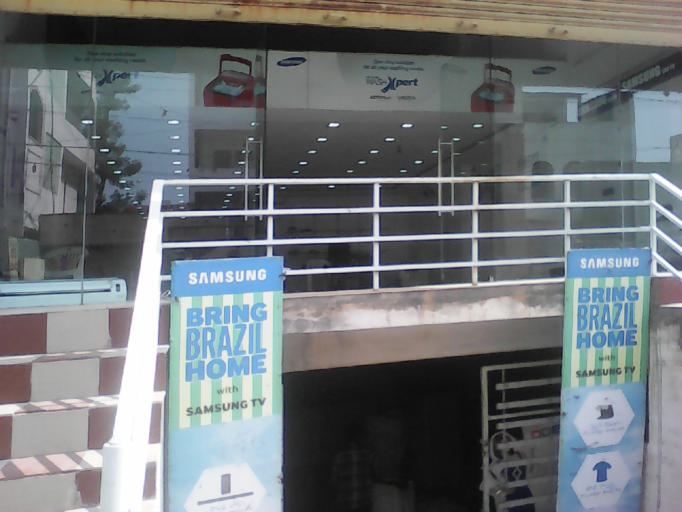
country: IN
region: Andhra Pradesh
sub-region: Guntur
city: Mangalagiri
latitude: 16.2409
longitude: 80.6495
